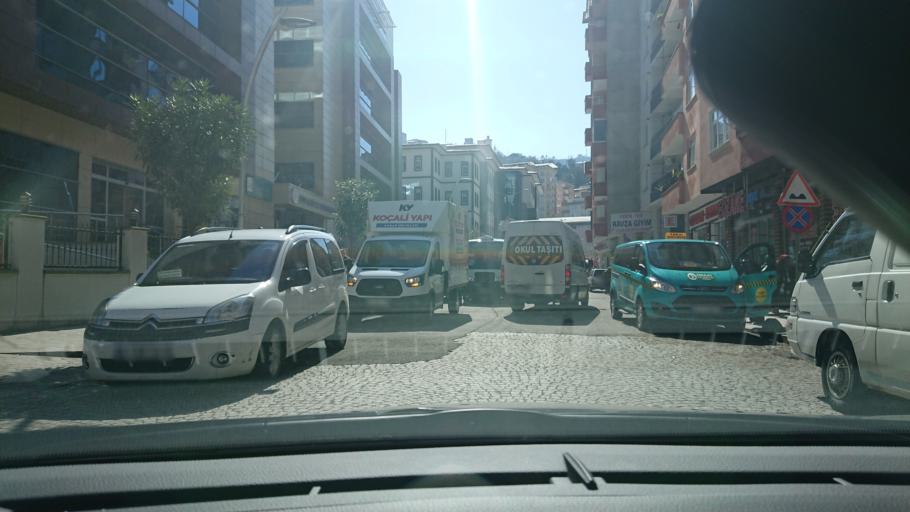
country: TR
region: Rize
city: Rize
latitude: 41.0232
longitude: 40.5282
